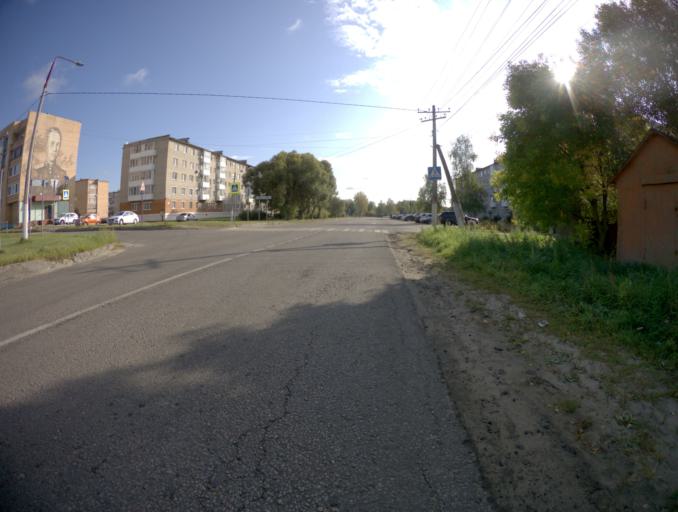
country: RU
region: Moskovskaya
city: Roshal'
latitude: 55.6589
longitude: 39.8509
